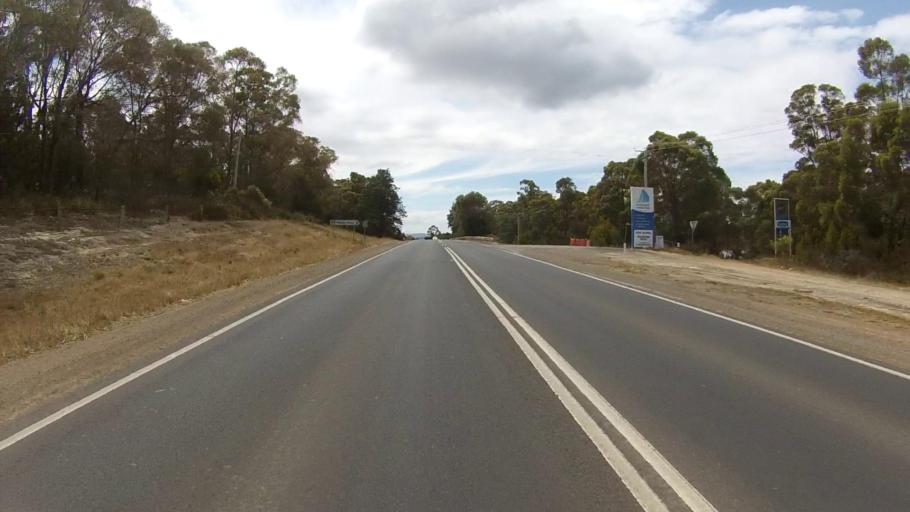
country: AU
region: Tasmania
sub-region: Kingborough
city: Margate
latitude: -43.0488
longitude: 147.2629
